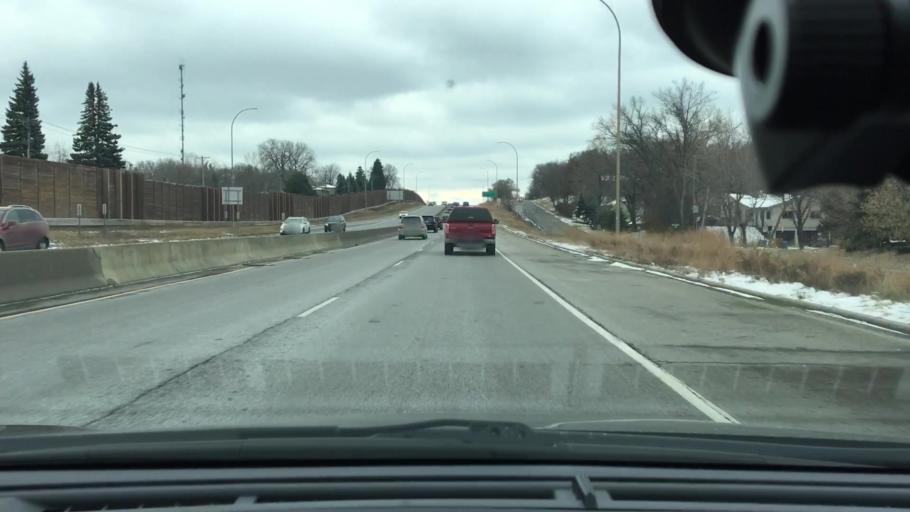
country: US
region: Minnesota
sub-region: Hennepin County
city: New Hope
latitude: 45.0055
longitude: -93.4010
